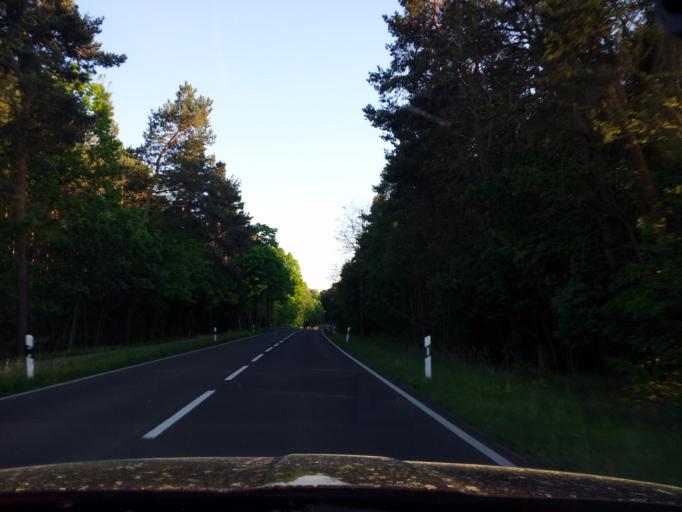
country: DE
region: Brandenburg
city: Luckenwalde
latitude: 52.0683
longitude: 13.1557
